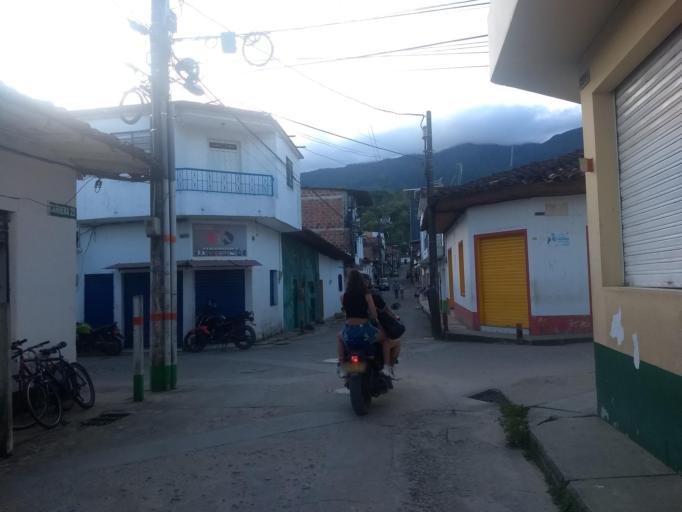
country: CO
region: Antioquia
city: San Carlos
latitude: 6.1873
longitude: -74.9937
